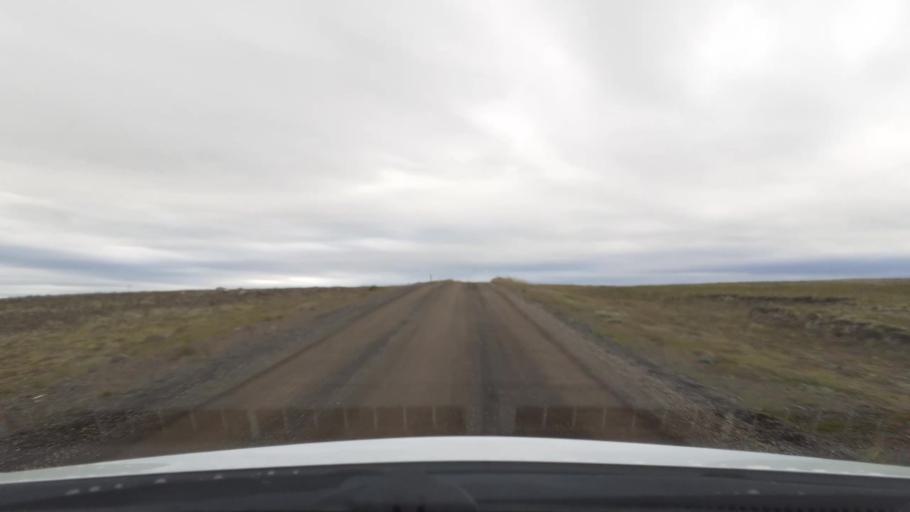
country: IS
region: Capital Region
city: Mosfellsbaer
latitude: 64.1968
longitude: -21.5524
